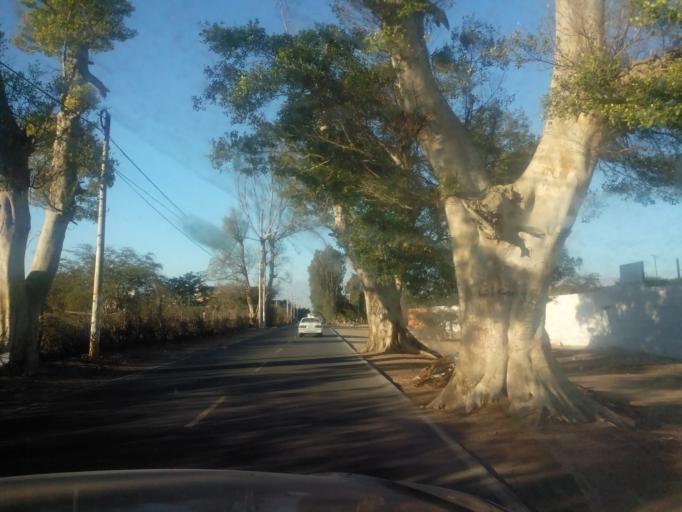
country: PE
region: Ica
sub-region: Provincia de Ica
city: Ica
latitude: -14.0833
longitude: -75.7525
